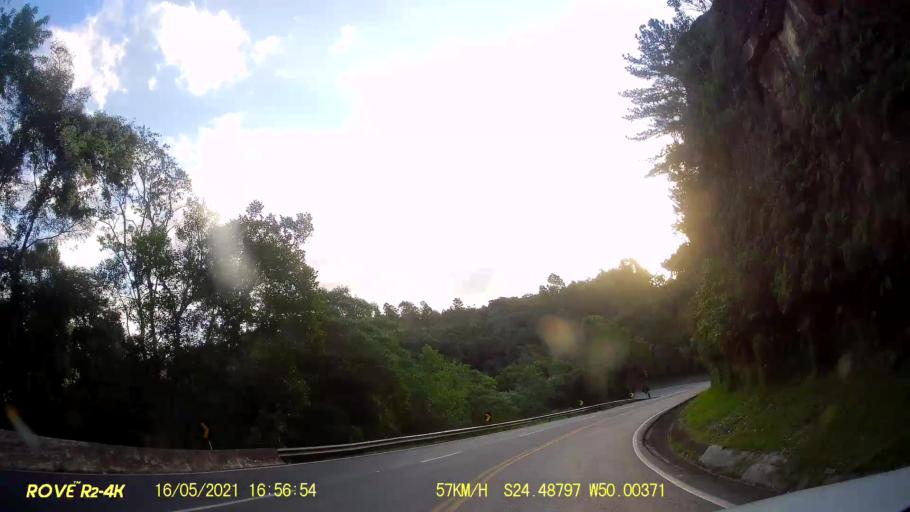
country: BR
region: Parana
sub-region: Pirai Do Sul
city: Pirai do Sul
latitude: -24.4880
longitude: -50.0038
